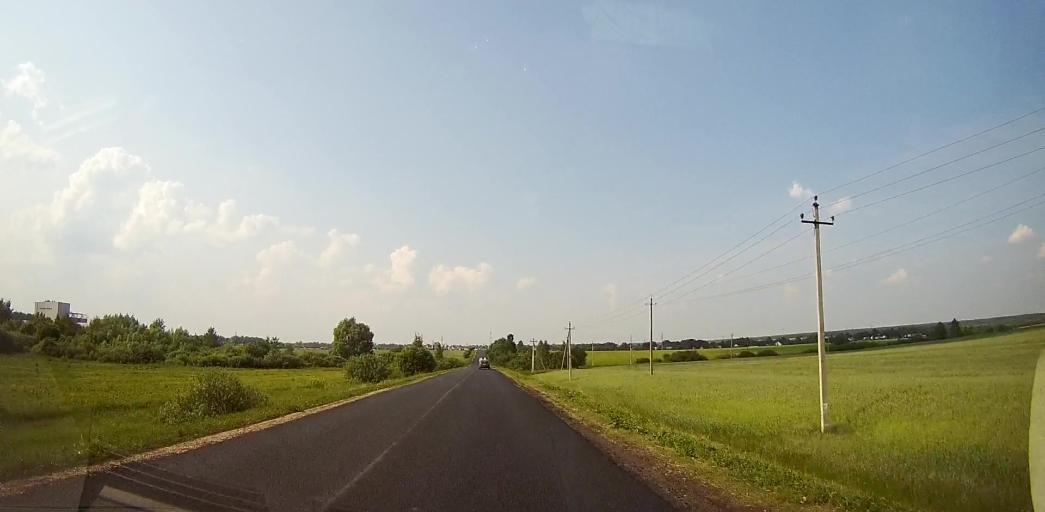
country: RU
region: Moskovskaya
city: Barybino
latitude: 55.2397
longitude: 37.9186
